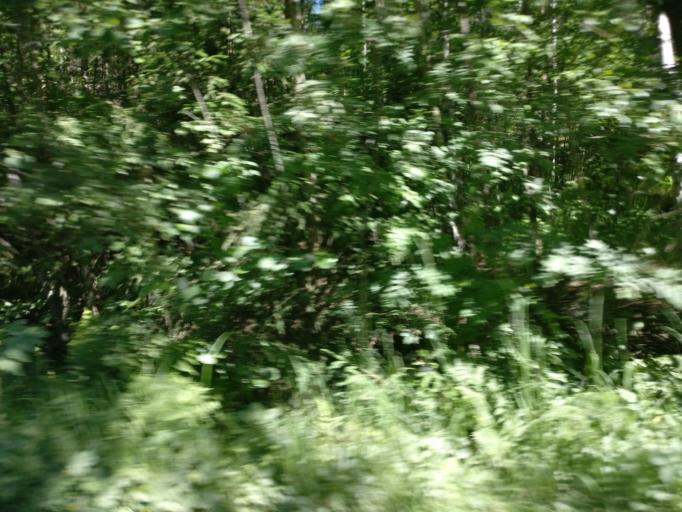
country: FI
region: Northern Savo
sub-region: Varkaus
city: Kangaslampi
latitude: 62.1770
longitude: 28.2366
